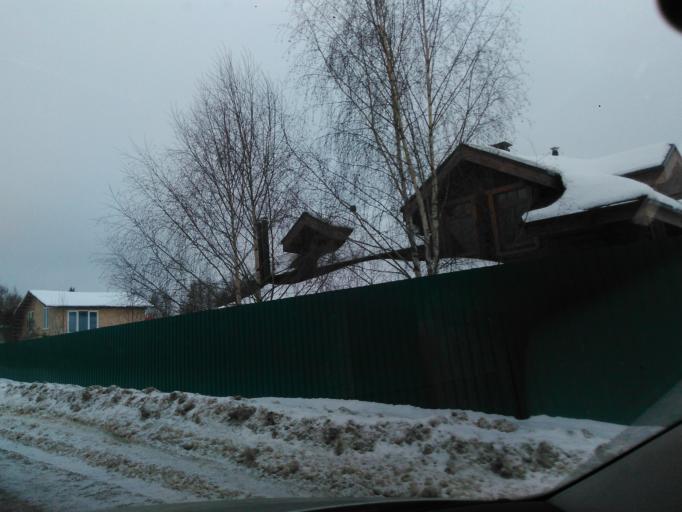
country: RU
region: Moskovskaya
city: Podosinki
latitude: 56.2771
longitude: 37.5926
